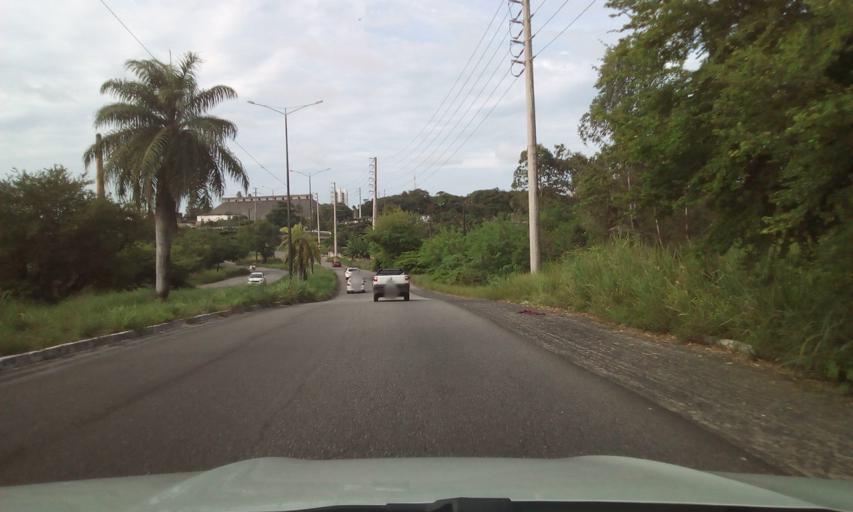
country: BR
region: Paraiba
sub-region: Joao Pessoa
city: Joao Pessoa
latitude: -7.1251
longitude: -34.8959
